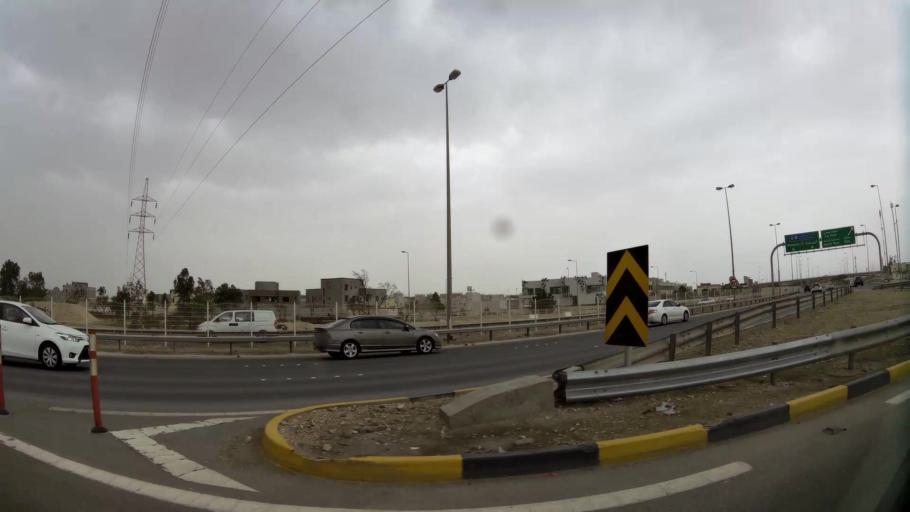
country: BH
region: Northern
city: Madinat `Isa
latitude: 26.1636
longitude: 50.5423
